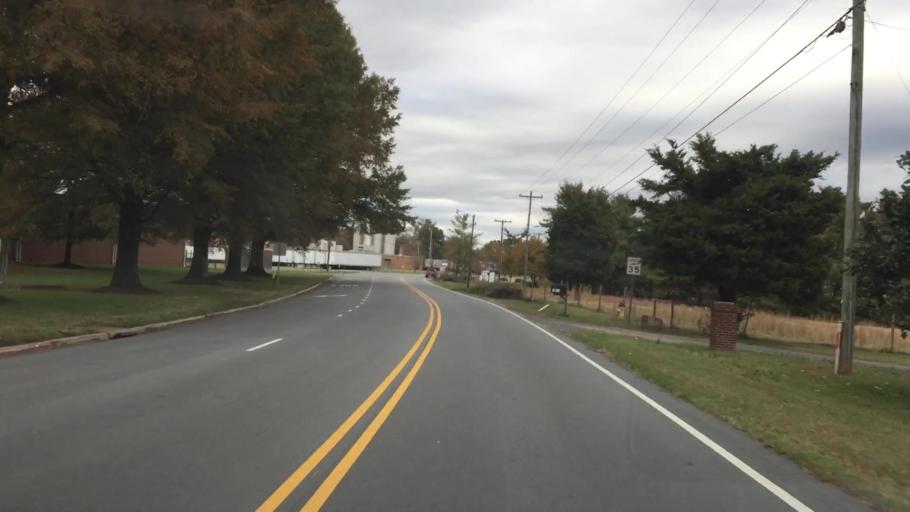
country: US
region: North Carolina
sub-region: Rockingham County
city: Reidsville
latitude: 36.3503
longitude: -79.6968
